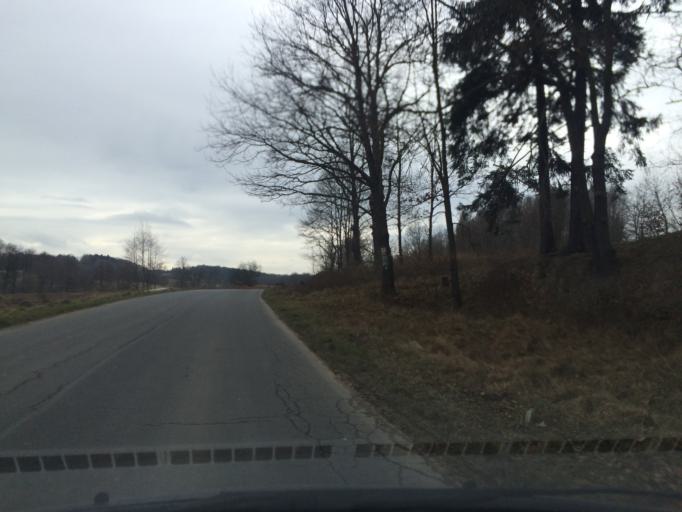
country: PL
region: Lower Silesian Voivodeship
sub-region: Powiat lwowecki
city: Lwowek Slaski
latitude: 51.1207
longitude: 15.5380
